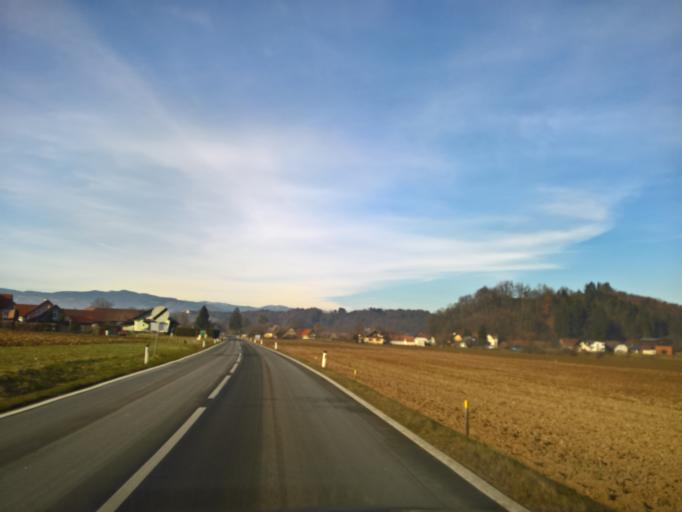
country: AT
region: Styria
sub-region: Politischer Bezirk Leibnitz
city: Oberhaag
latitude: 46.6954
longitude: 15.3133
